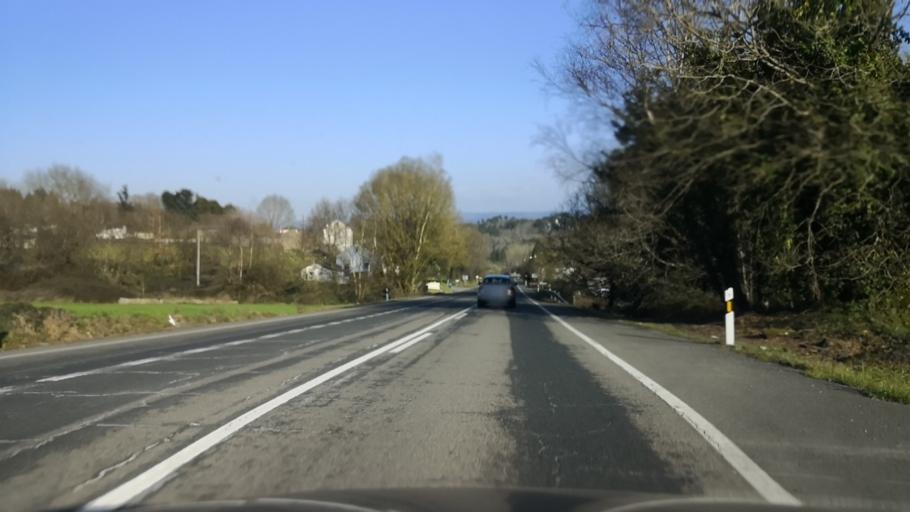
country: ES
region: Galicia
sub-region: Provincia de Lugo
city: Corgo
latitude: 42.9642
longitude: -7.4911
